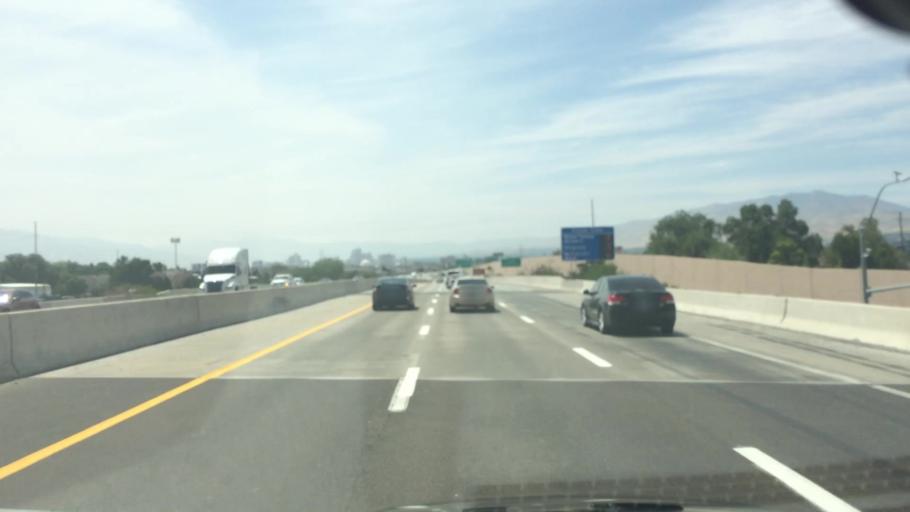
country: US
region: Nevada
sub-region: Washoe County
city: Sparks
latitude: 39.5340
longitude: -119.7651
